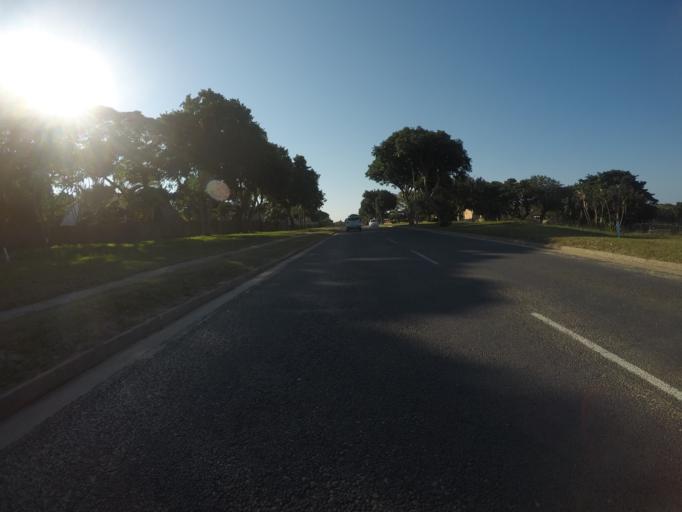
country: ZA
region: KwaZulu-Natal
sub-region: uThungulu District Municipality
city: Richards Bay
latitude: -28.7901
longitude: 32.0985
